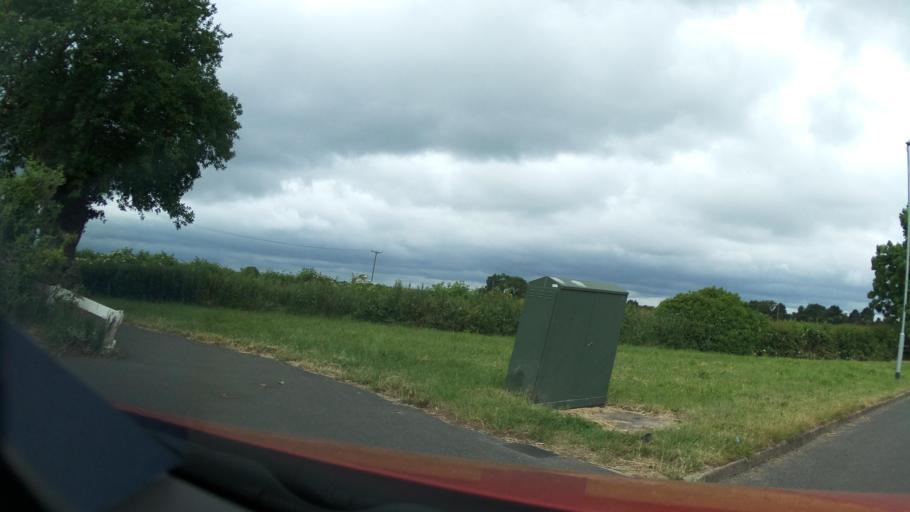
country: GB
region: England
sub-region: Leicestershire
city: Coalville
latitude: 52.7318
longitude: -1.3487
